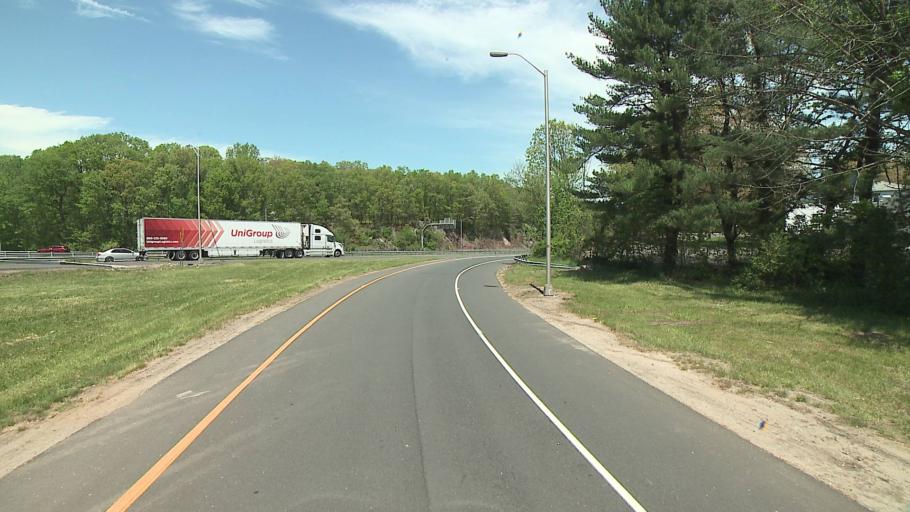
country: US
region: Connecticut
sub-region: New Haven County
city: Waterbury
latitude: 41.5484
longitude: -73.0620
